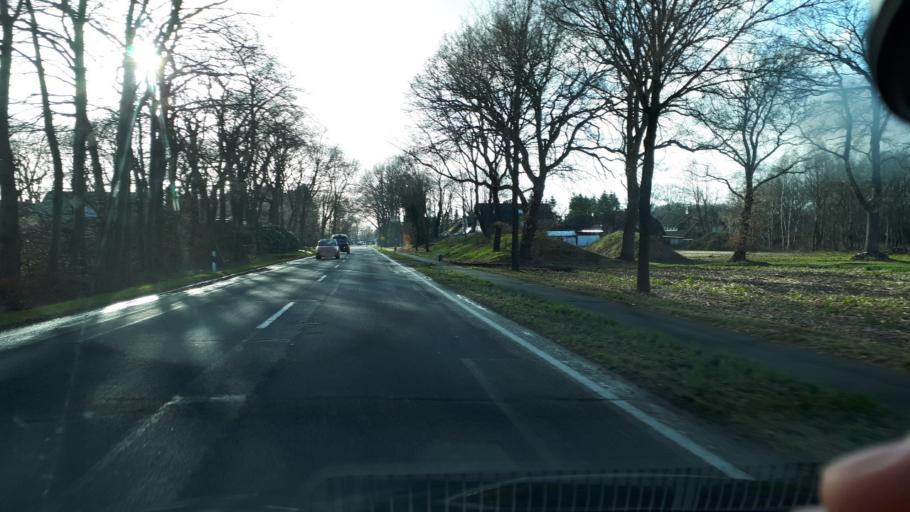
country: DE
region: Lower Saxony
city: Vrees
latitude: 52.8821
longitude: 7.8493
